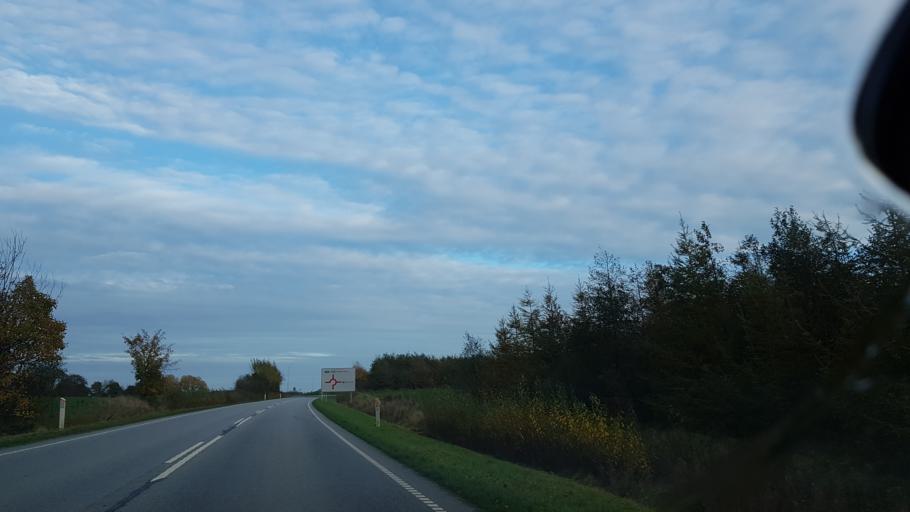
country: DK
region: South Denmark
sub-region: Haderslev Kommune
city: Haderslev
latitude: 55.2958
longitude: 9.4200
